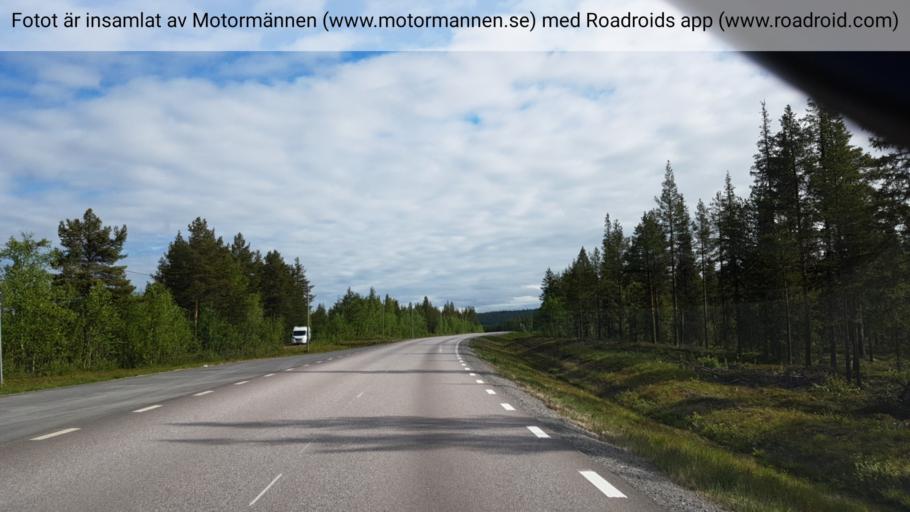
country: SE
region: Norrbotten
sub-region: Gallivare Kommun
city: Malmberget
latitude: 67.4683
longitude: 21.1241
